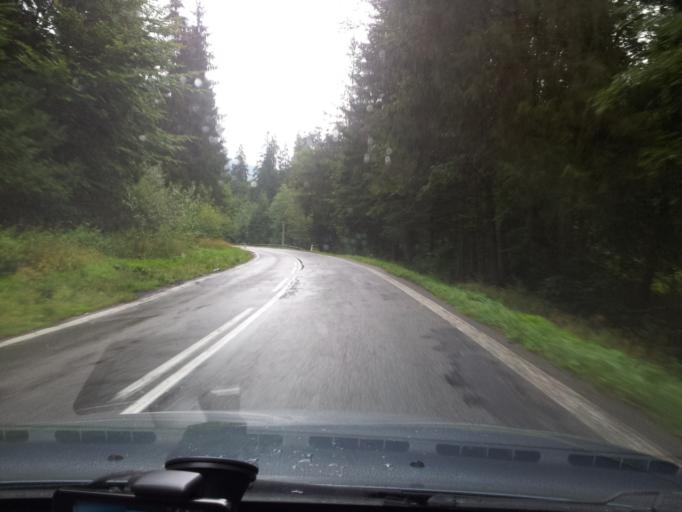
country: SK
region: Banskobystricky
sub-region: Okres Banska Bystrica
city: Brezno
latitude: 48.8698
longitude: 19.6519
